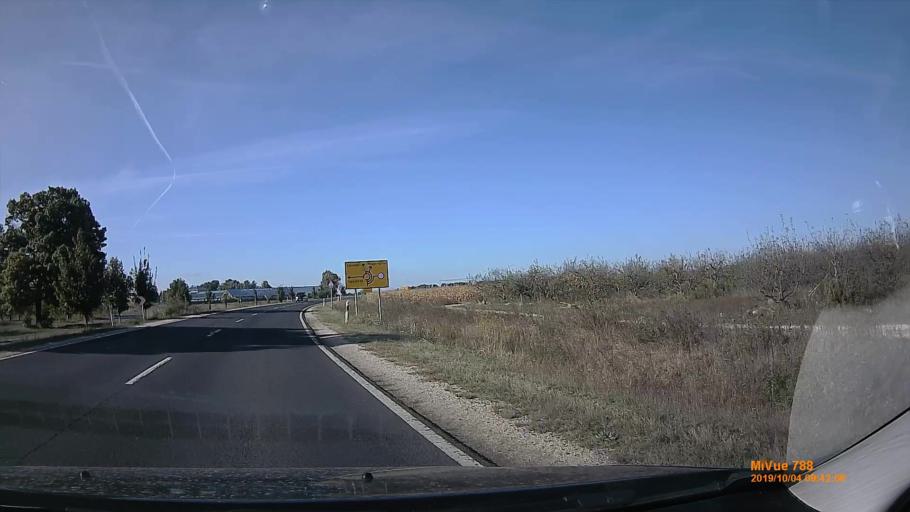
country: HU
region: Somogy
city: Kaposvar
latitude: 46.4264
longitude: 17.7786
